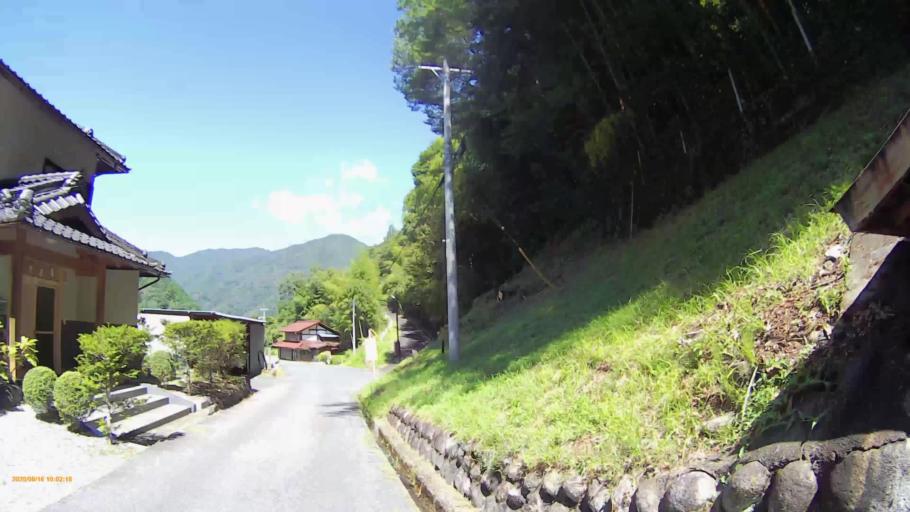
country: JP
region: Nagano
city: Iida
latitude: 35.6831
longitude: 137.6679
